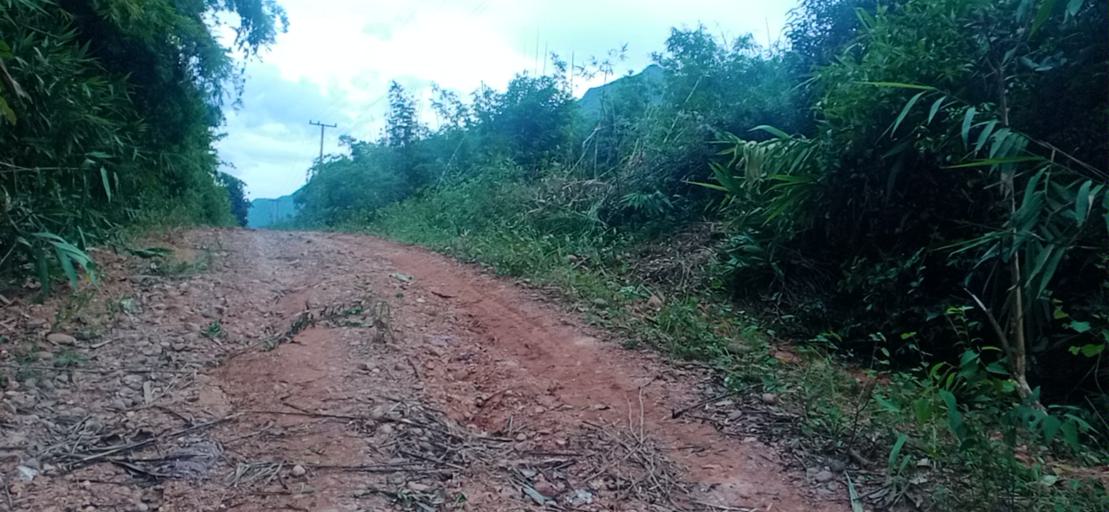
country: TH
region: Changwat Bueng Kan
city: Pak Khat
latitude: 18.5603
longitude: 103.2262
